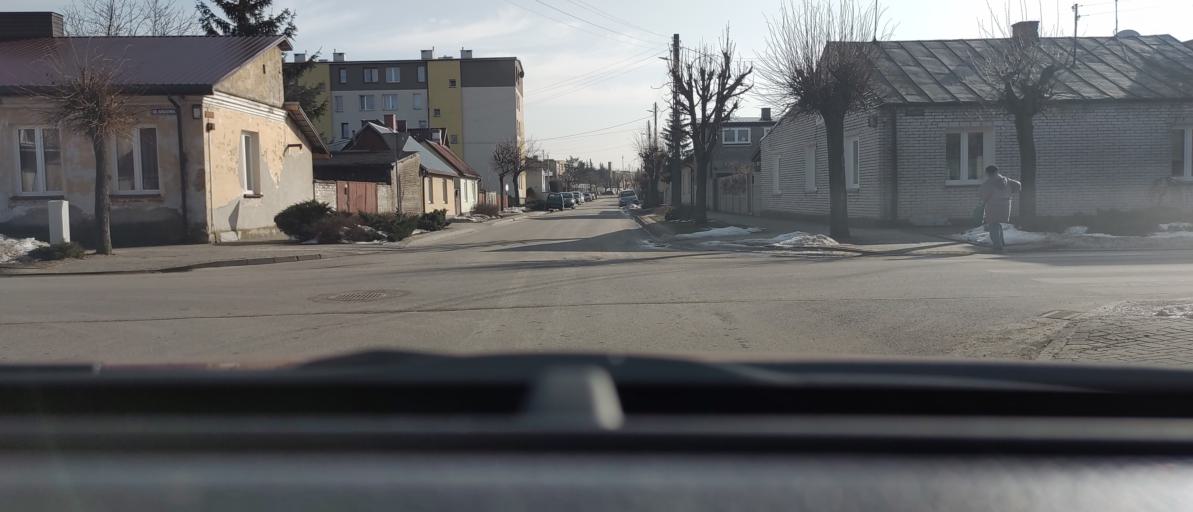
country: PL
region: Masovian Voivodeship
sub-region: Powiat bialobrzeski
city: Bialobrzegi
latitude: 51.6473
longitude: 20.9514
